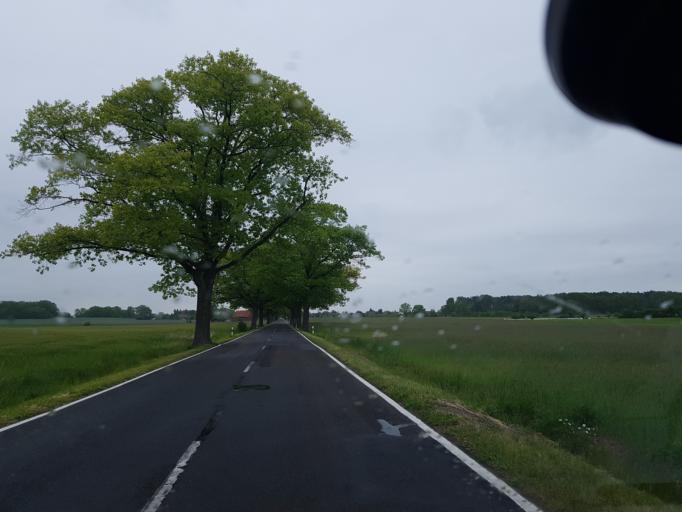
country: DE
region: Brandenburg
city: Cottbus
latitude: 51.6708
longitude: 14.3494
